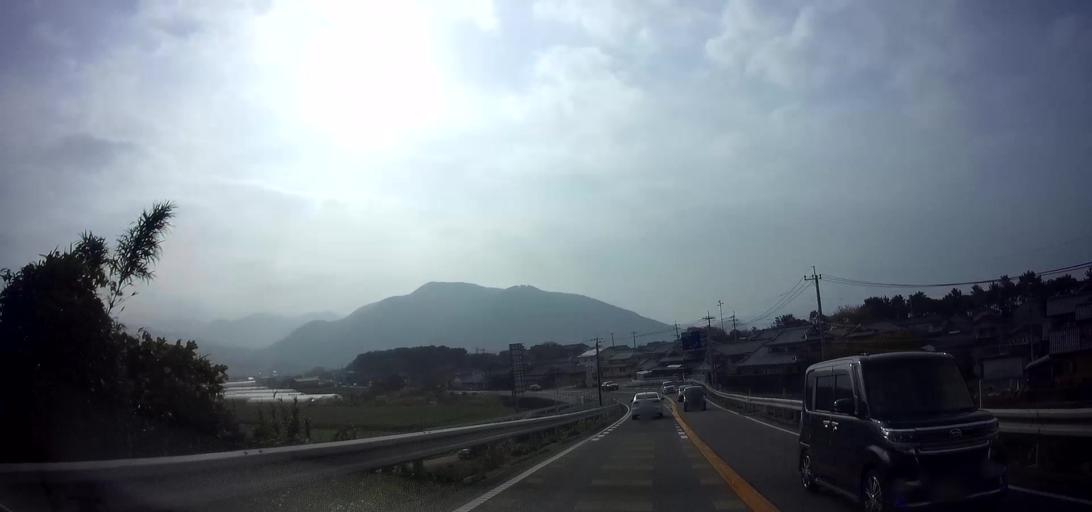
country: JP
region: Nagasaki
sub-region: Isahaya-shi
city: Isahaya
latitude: 32.7942
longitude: 130.1833
